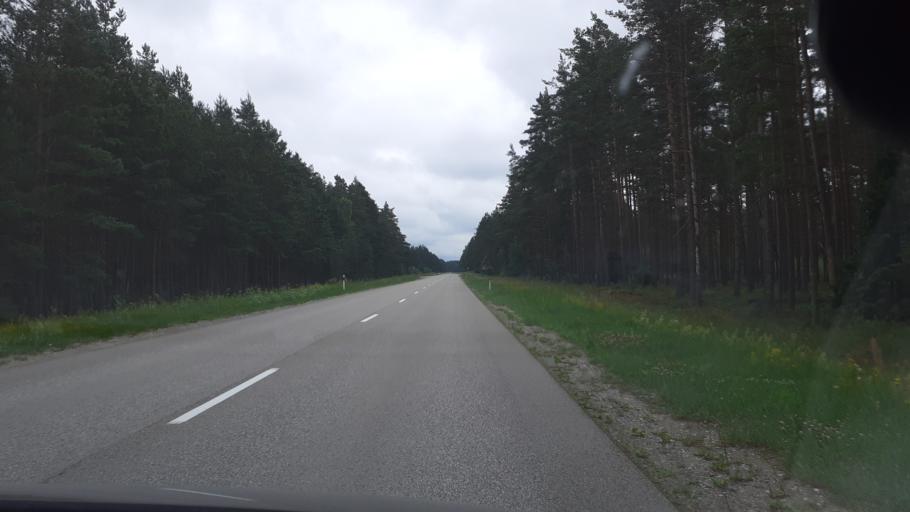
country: LV
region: Ventspils Rajons
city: Piltene
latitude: 57.1287
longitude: 21.7336
